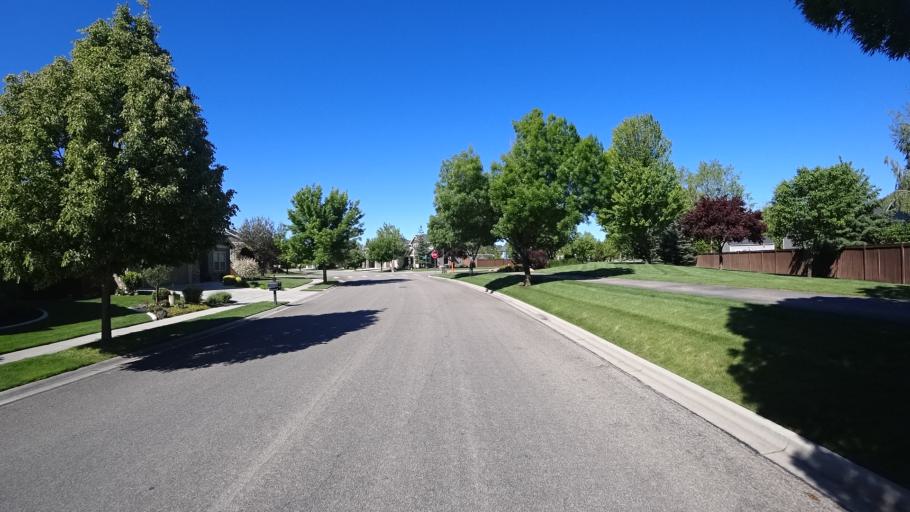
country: US
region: Idaho
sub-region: Ada County
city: Meridian
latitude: 43.6574
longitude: -116.4048
